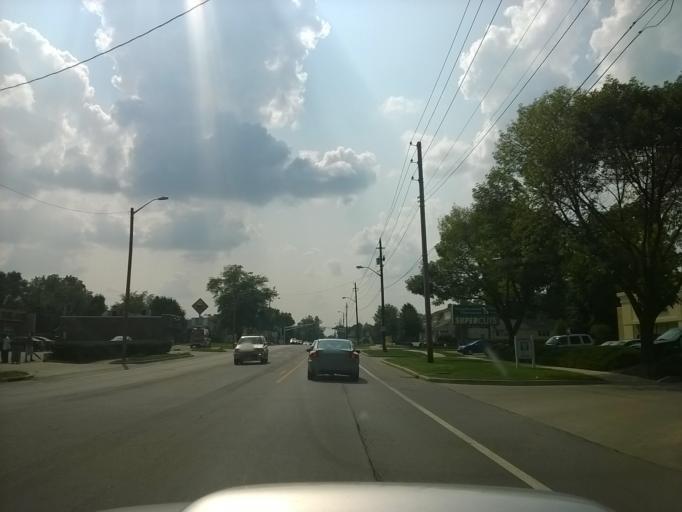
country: US
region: Indiana
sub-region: Marion County
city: Broad Ripple
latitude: 39.8687
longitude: -86.1246
